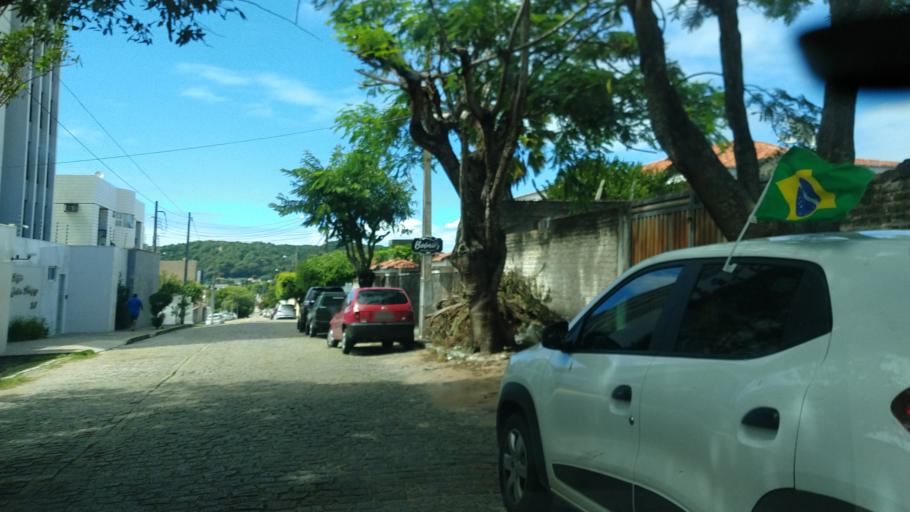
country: BR
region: Rio Grande do Norte
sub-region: Natal
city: Natal
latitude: -5.8202
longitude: -35.2046
